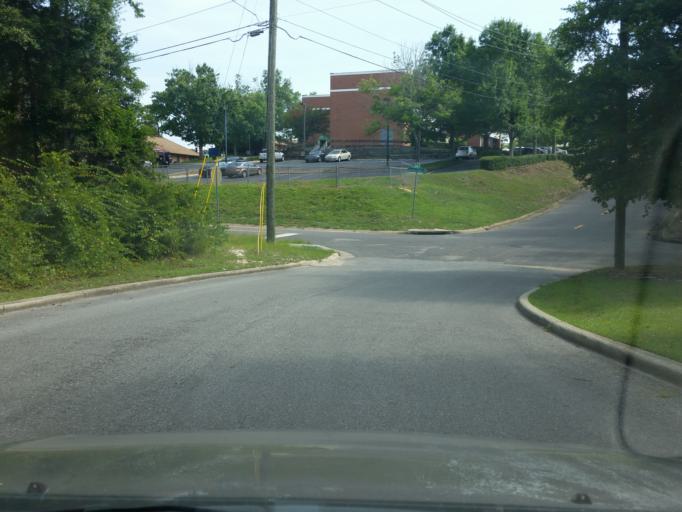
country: US
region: Florida
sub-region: Escambia County
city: Brent
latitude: 30.4704
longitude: -87.2100
